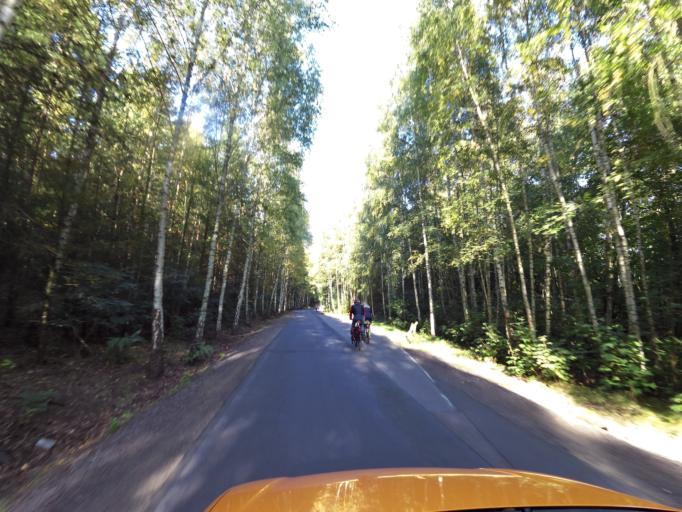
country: DE
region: Berlin
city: Kladow
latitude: 52.4377
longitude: 13.1086
